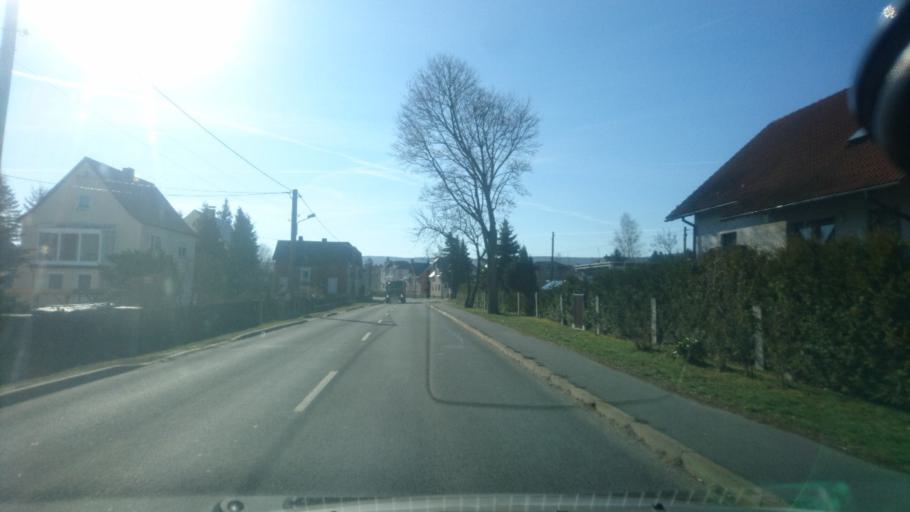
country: DE
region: Saxony
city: Bergen
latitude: 50.4738
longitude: 12.2666
